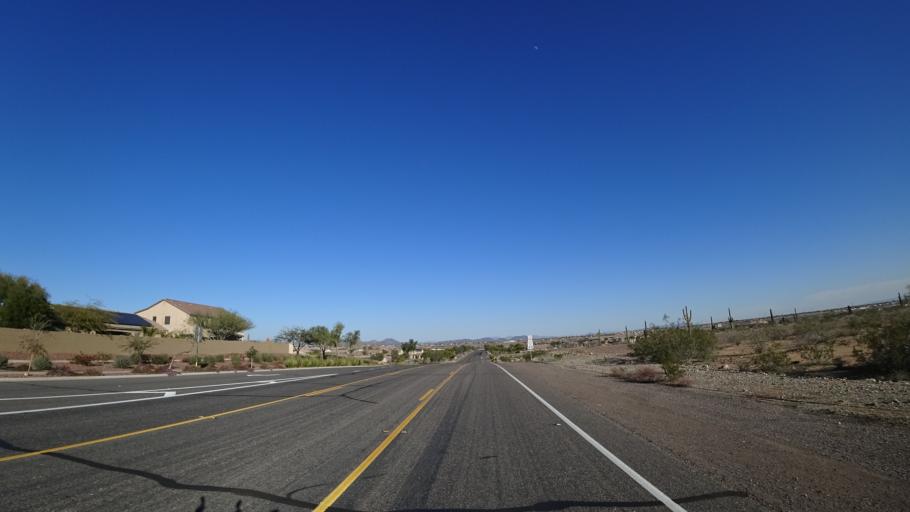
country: US
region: Arizona
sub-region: Maricopa County
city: Sun City West
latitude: 33.6893
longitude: -112.3205
